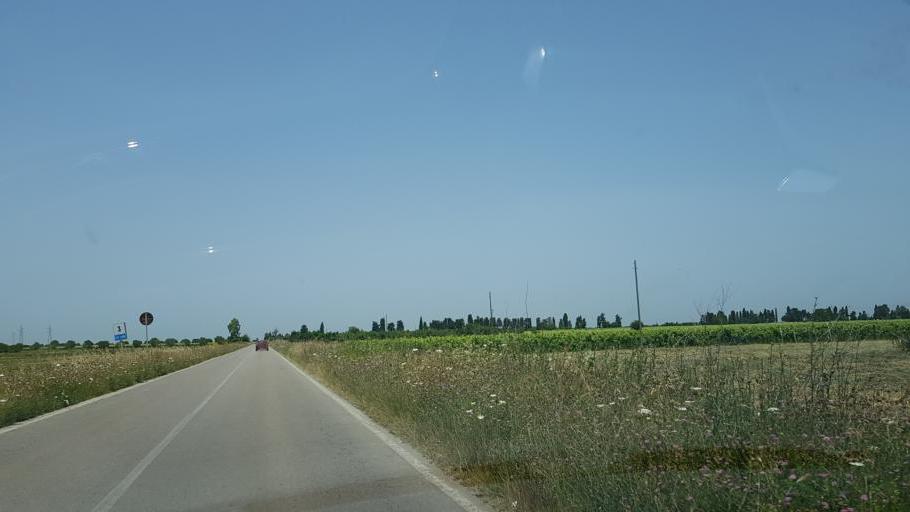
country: IT
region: Apulia
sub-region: Provincia di Brindisi
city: San Pancrazio Salentino
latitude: 40.3797
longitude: 17.8372
